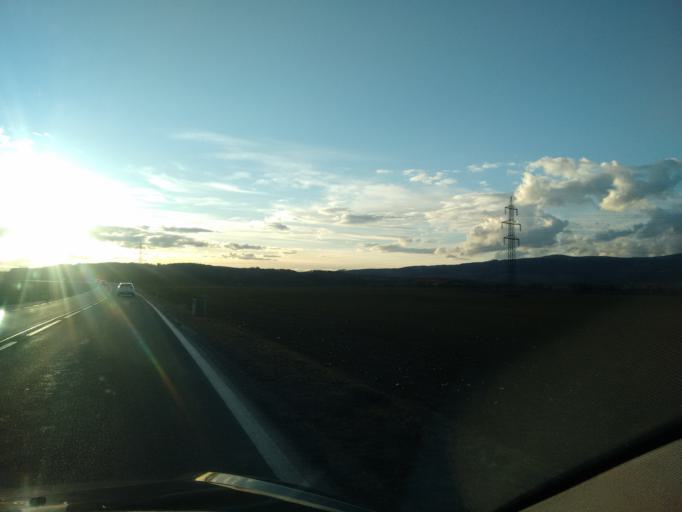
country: AT
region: Lower Austria
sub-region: Politischer Bezirk Melk
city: Pochlarn
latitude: 48.1939
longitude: 15.2024
